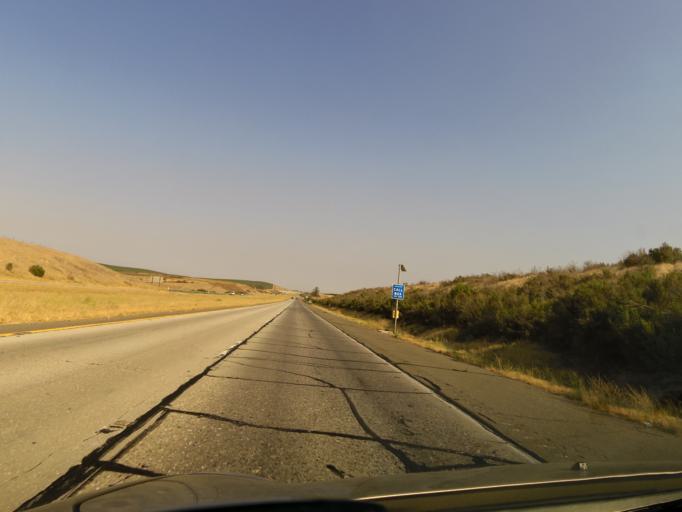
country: US
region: California
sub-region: Monterey County
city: King City
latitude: 36.0844
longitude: -121.0087
